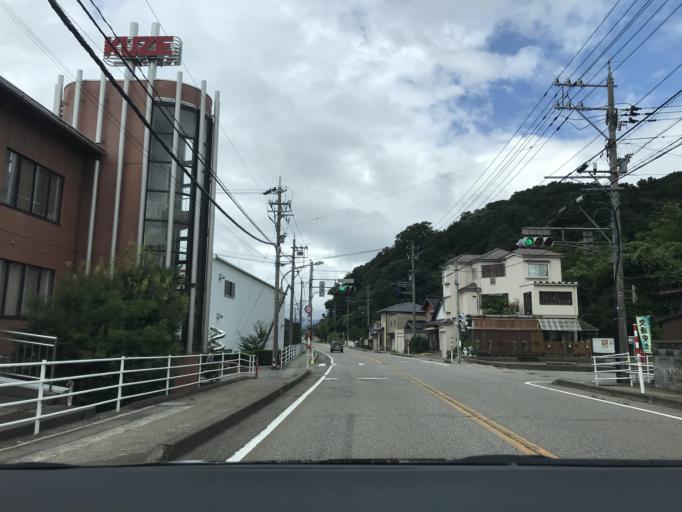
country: JP
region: Ishikawa
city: Tsubata
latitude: 36.6539
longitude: 136.7289
